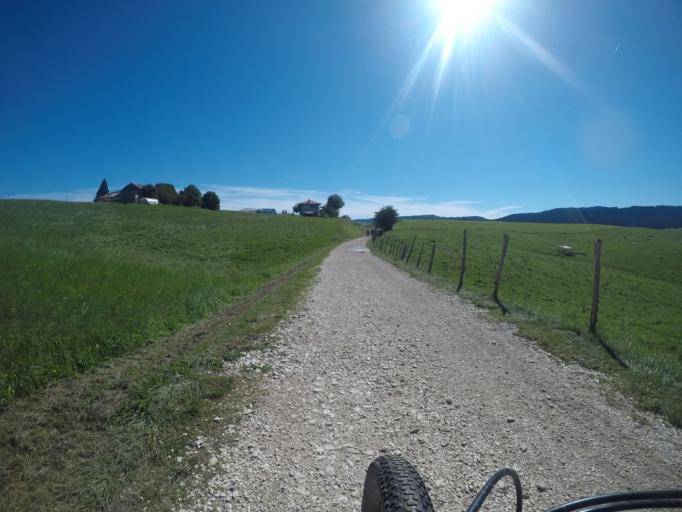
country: IT
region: Veneto
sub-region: Provincia di Vicenza
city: Canove di Roana
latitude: 45.8671
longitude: 11.4897
